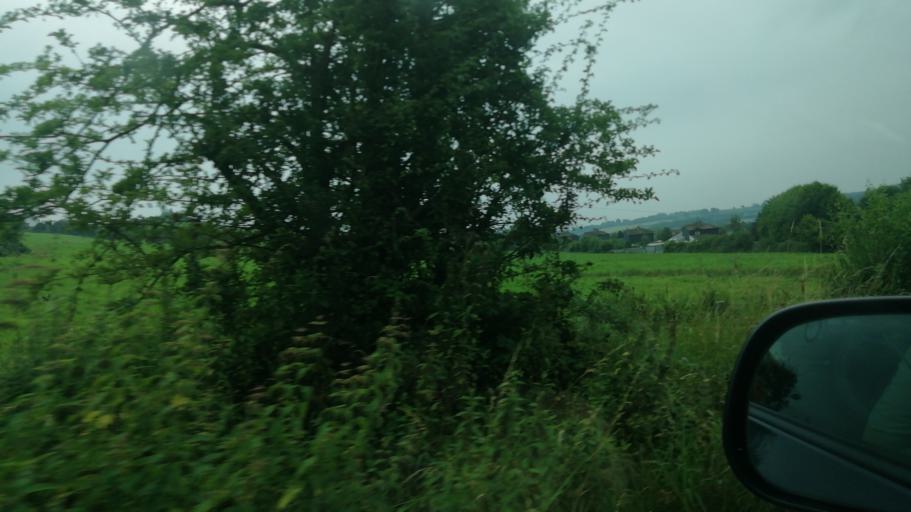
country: IE
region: Munster
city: Fethard
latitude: 52.5735
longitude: -7.6634
